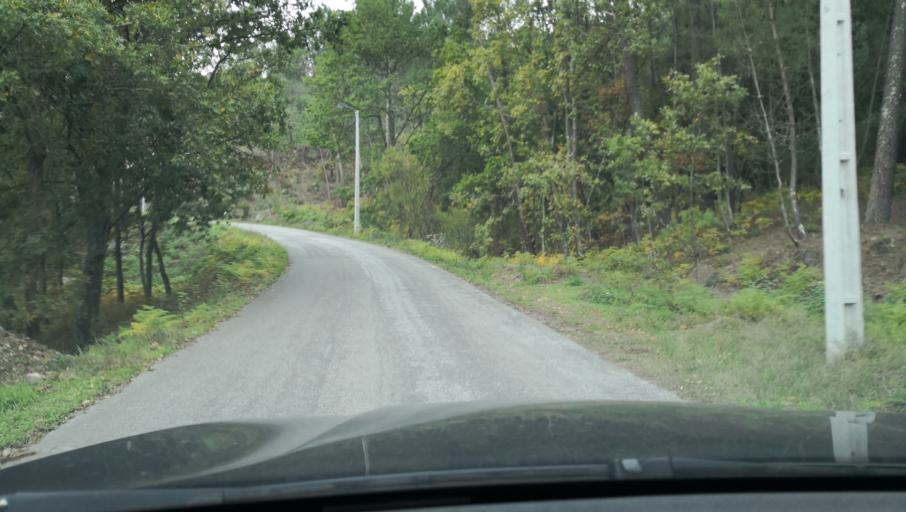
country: PT
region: Vila Real
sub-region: Vila Real
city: Vila Real
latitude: 41.3223
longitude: -7.7560
